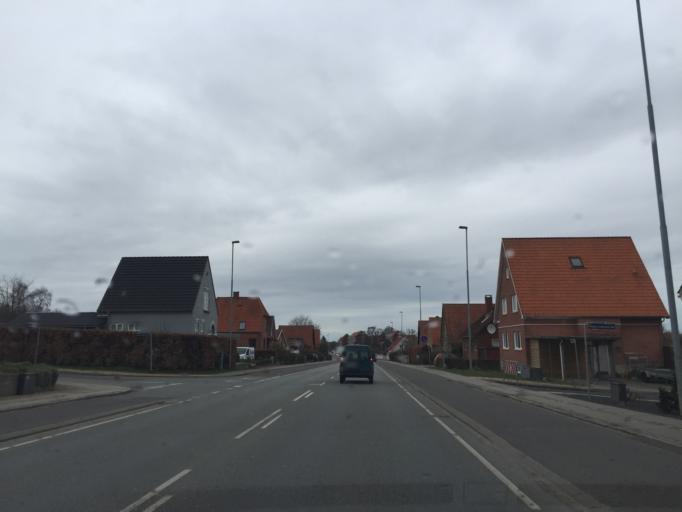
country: DK
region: South Denmark
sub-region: Odense Kommune
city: Odense
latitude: 55.3950
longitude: 10.3392
